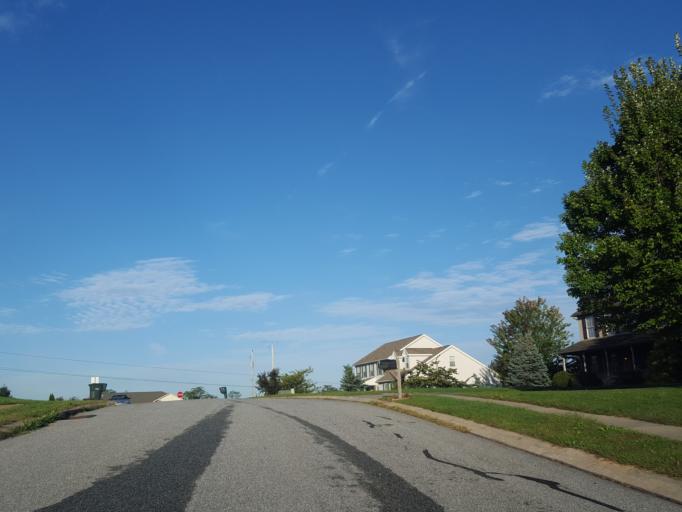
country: US
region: Pennsylvania
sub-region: York County
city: Windsor
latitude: 39.9509
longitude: -76.6043
